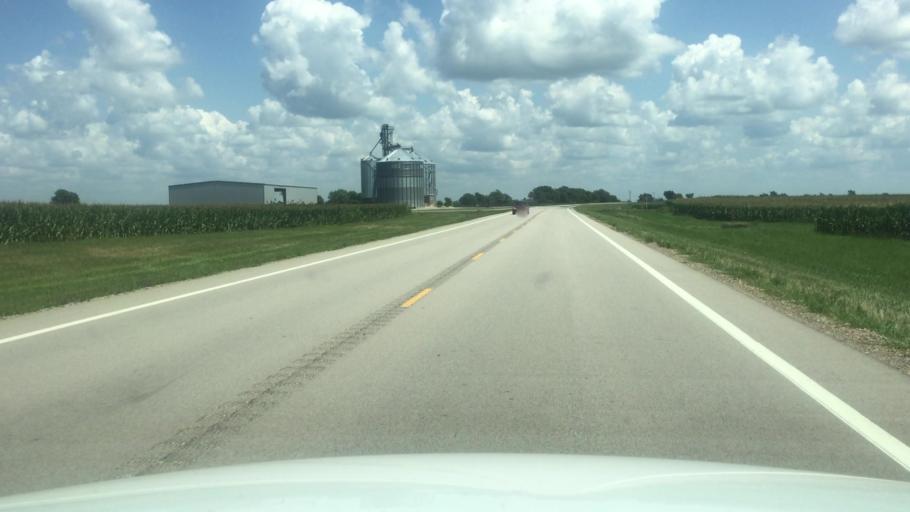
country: US
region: Kansas
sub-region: Brown County
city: Horton
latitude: 39.6603
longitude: -95.3889
